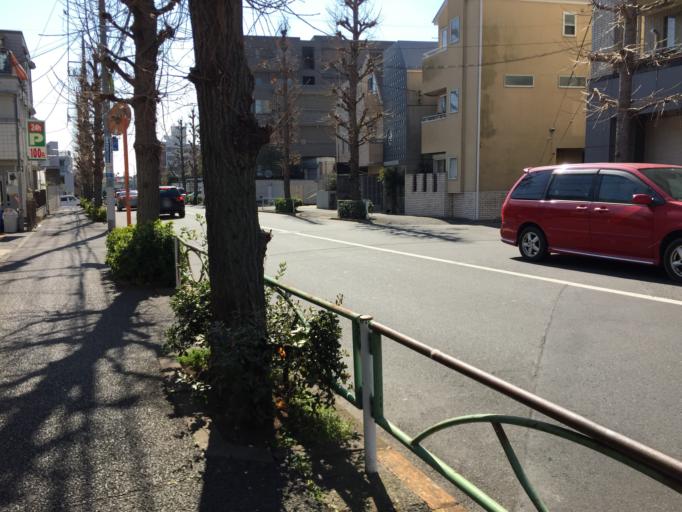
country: JP
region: Tokyo
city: Tokyo
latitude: 35.6126
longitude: 139.6527
